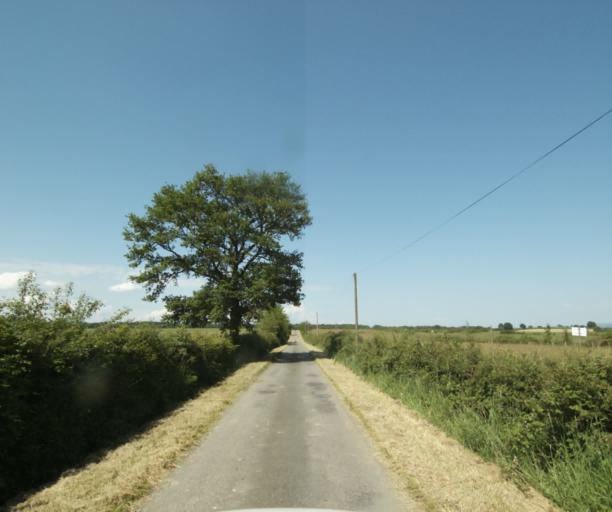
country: FR
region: Bourgogne
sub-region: Departement de Saone-et-Loire
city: Palinges
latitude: 46.5652
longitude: 4.1918
